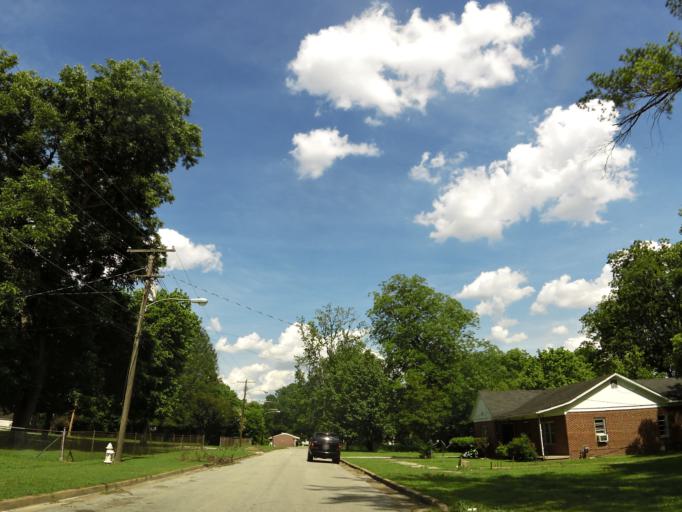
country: US
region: Tennessee
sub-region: Gibson County
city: Trenton
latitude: 35.9797
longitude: -88.9392
